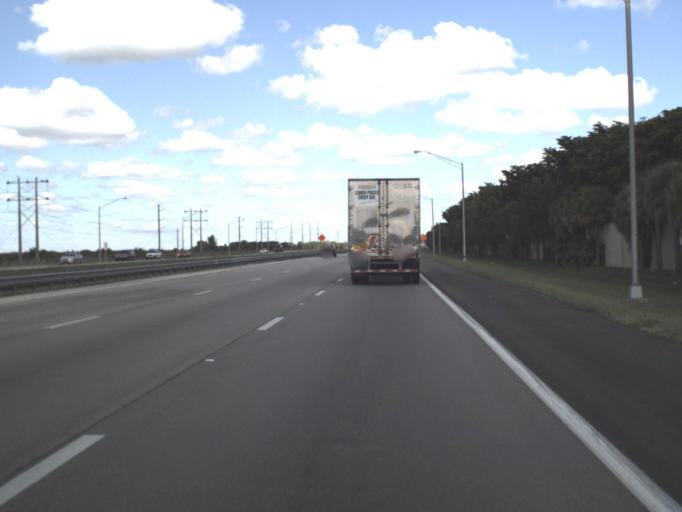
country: US
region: Florida
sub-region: Broward County
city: Tamarac
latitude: 26.2212
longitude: -80.2963
